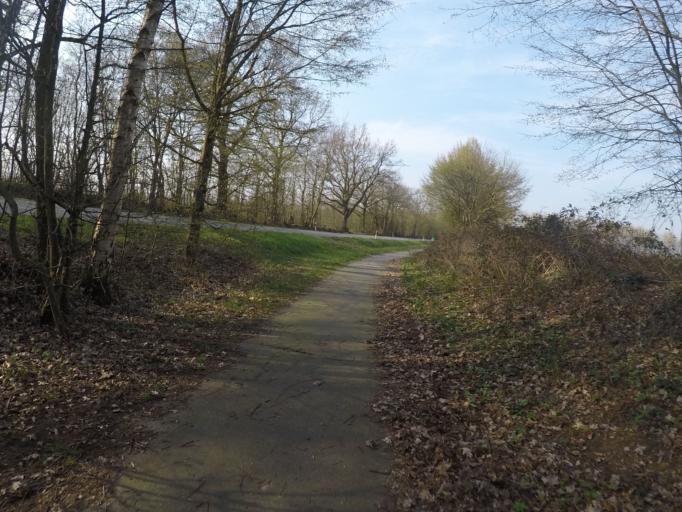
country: DE
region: Schleswig-Holstein
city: Kukels
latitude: 53.9138
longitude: 10.2228
